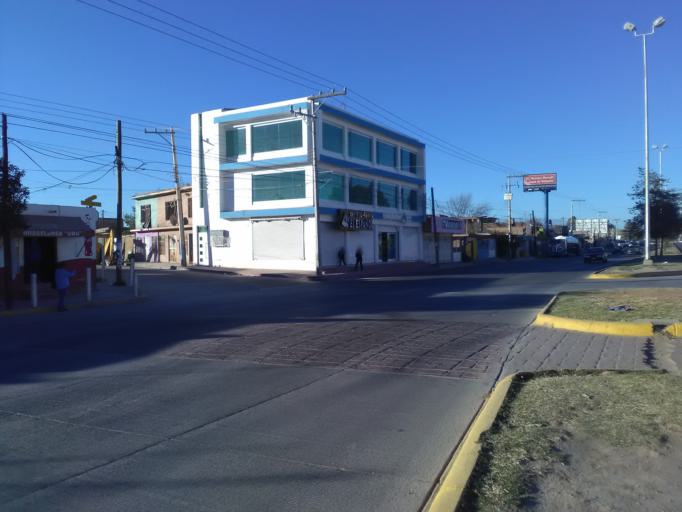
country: MX
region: Durango
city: Victoria de Durango
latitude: 24.0470
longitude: -104.6520
